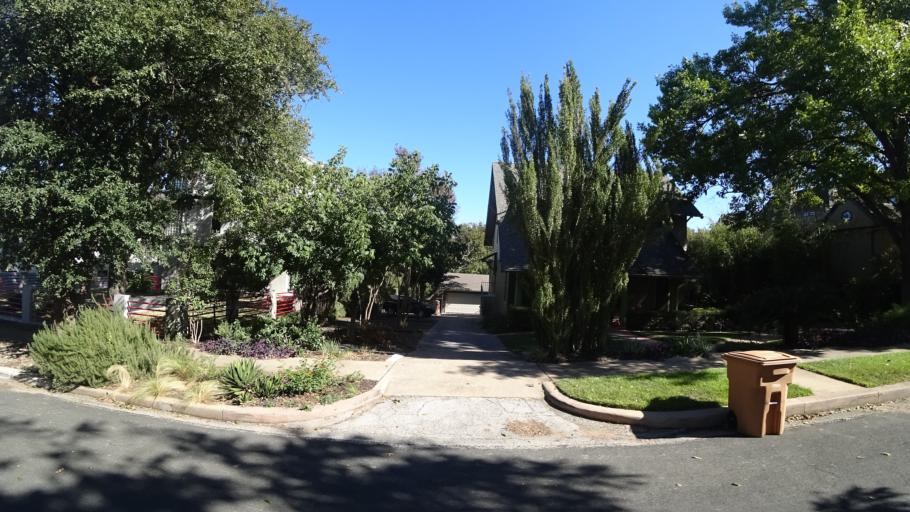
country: US
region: Texas
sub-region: Travis County
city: Austin
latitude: 30.2784
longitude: -97.7530
